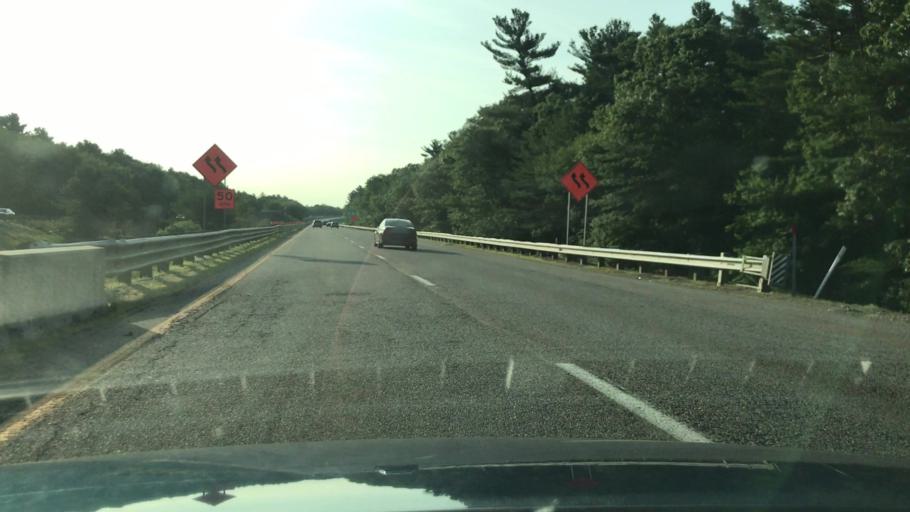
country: US
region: Massachusetts
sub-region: Plymouth County
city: Rockland
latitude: 42.1578
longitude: -70.8693
